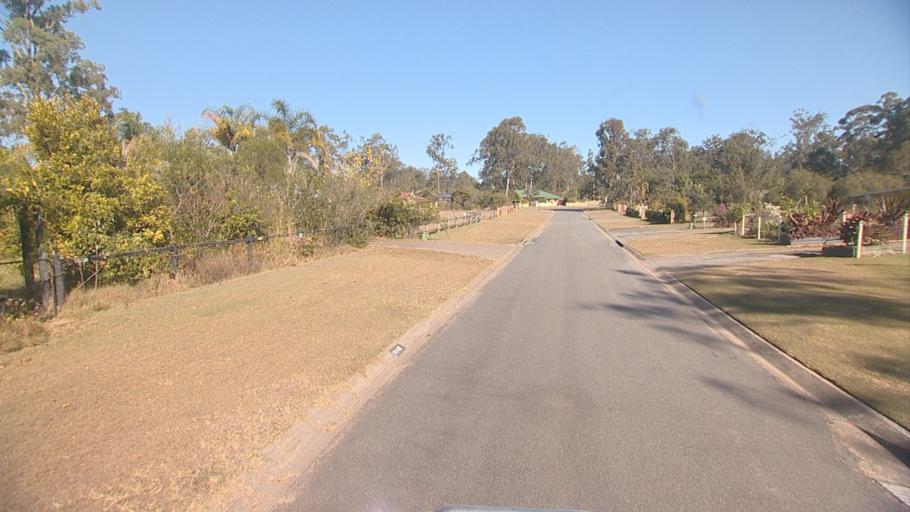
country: AU
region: Queensland
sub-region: Logan
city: North Maclean
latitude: -27.8163
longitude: 152.9505
